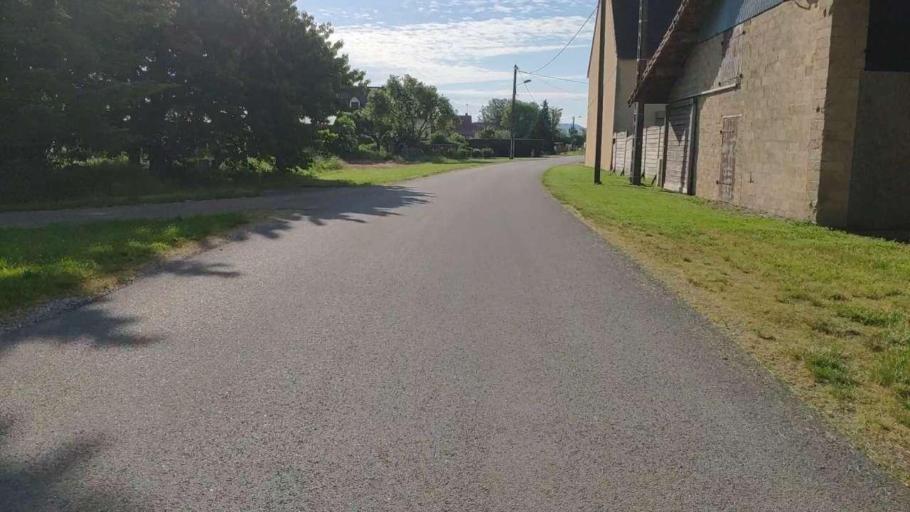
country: FR
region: Franche-Comte
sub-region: Departement du Jura
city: Bletterans
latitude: 46.7400
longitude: 5.4646
